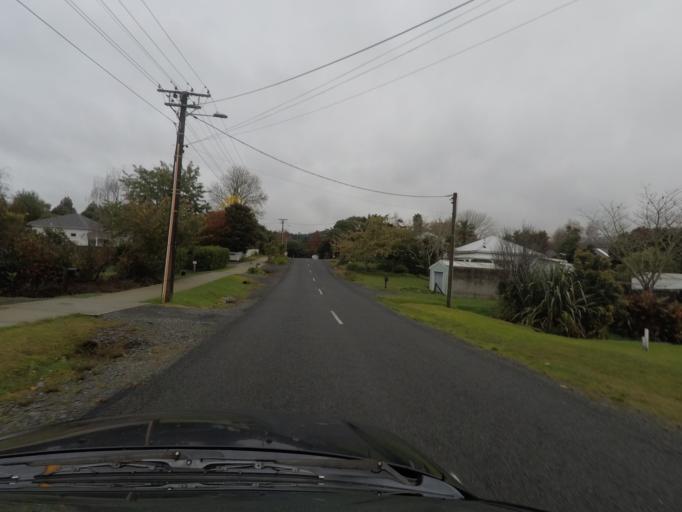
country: NZ
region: Auckland
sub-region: Auckland
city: Rosebank
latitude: -36.7555
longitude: 174.5958
